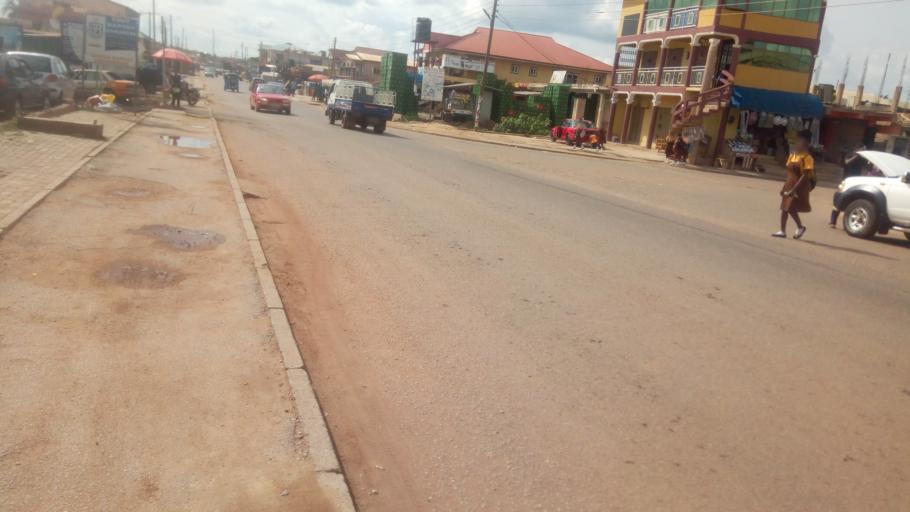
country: GH
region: Ashanti
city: Obuasi
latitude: 6.2072
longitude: -1.6833
